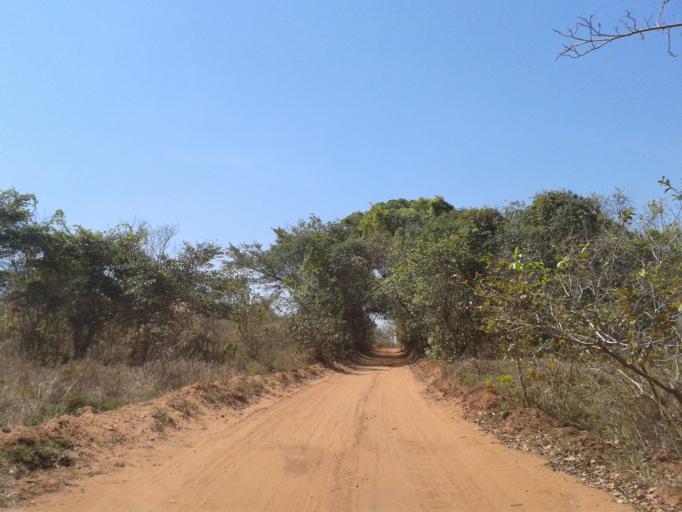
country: BR
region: Minas Gerais
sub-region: Ituiutaba
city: Ituiutaba
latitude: -19.0973
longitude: -49.2980
